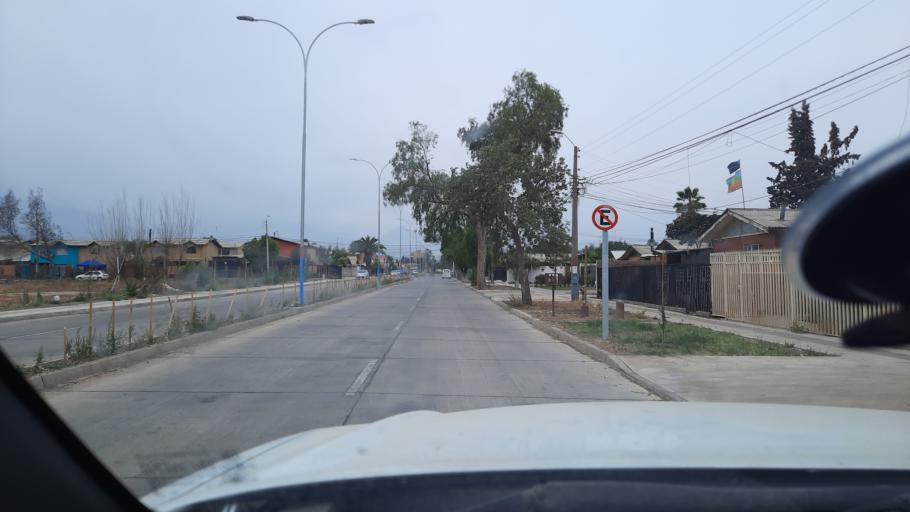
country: CL
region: Valparaiso
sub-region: Provincia de San Felipe
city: San Felipe
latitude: -32.7430
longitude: -70.7200
